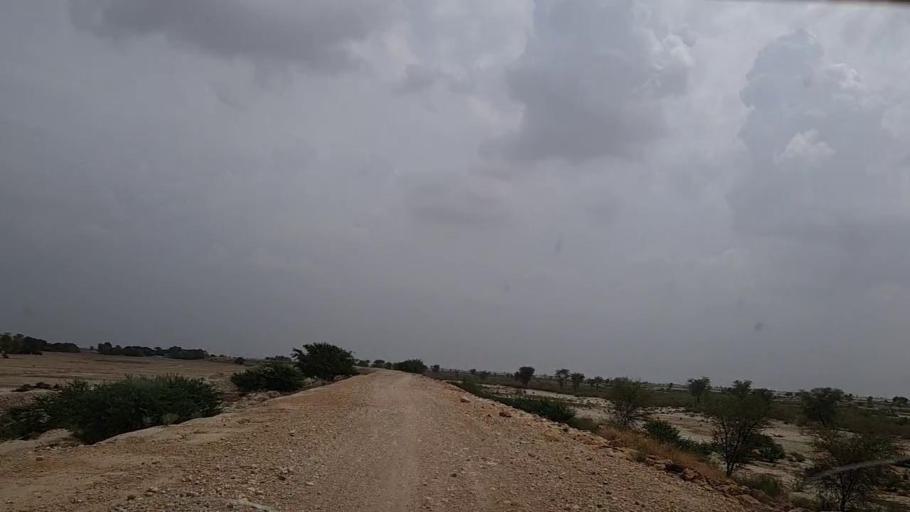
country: PK
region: Sindh
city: Johi
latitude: 26.7279
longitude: 67.5781
